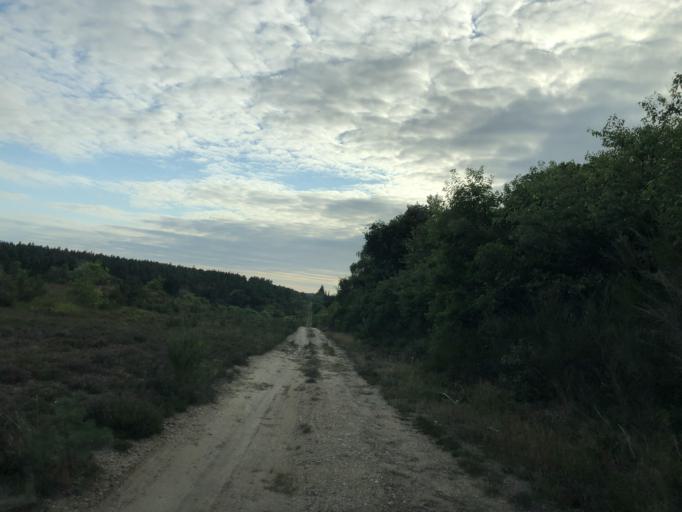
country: DK
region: Central Jutland
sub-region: Holstebro Kommune
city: Ulfborg
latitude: 56.2897
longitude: 8.4215
